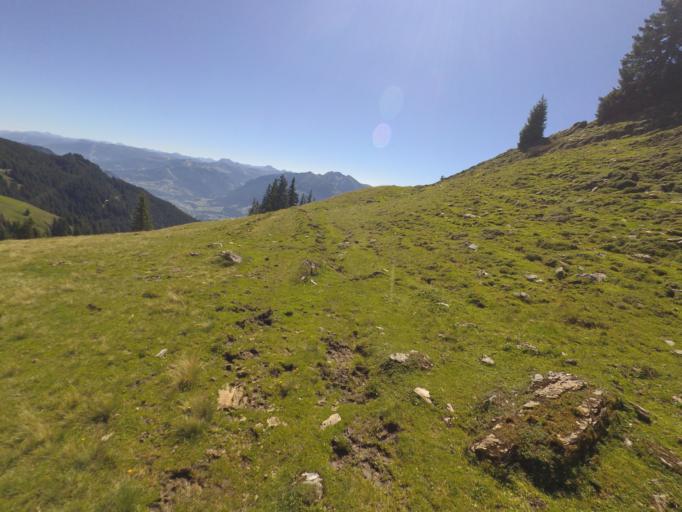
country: AT
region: Salzburg
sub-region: Politischer Bezirk Sankt Johann im Pongau
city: Goldegg
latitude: 47.3479
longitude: 13.0670
